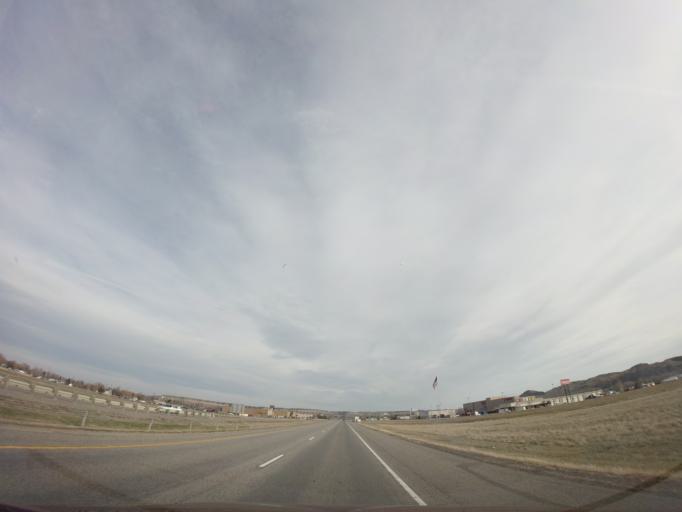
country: US
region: Montana
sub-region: Yellowstone County
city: Billings
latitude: 45.7521
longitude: -108.5320
